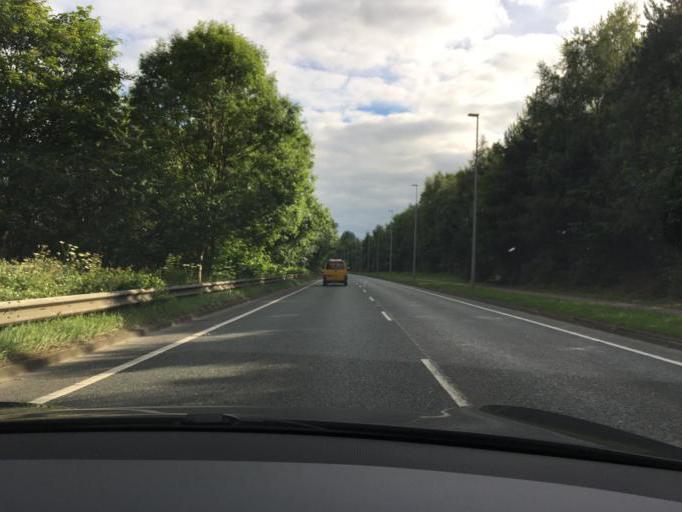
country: GB
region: England
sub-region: City and Borough of Salford
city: Irlam
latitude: 53.4538
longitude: -2.4036
